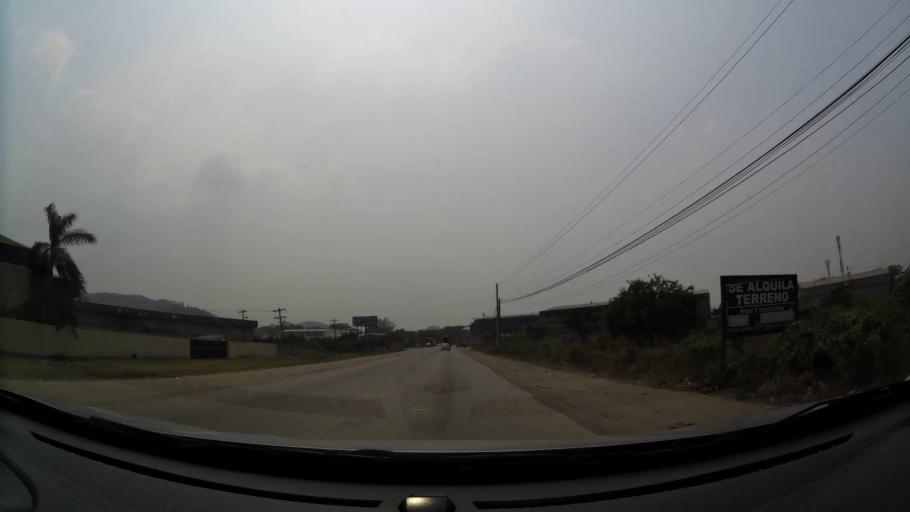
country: HN
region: Cortes
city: Chotepe
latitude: 15.4633
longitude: -87.9679
